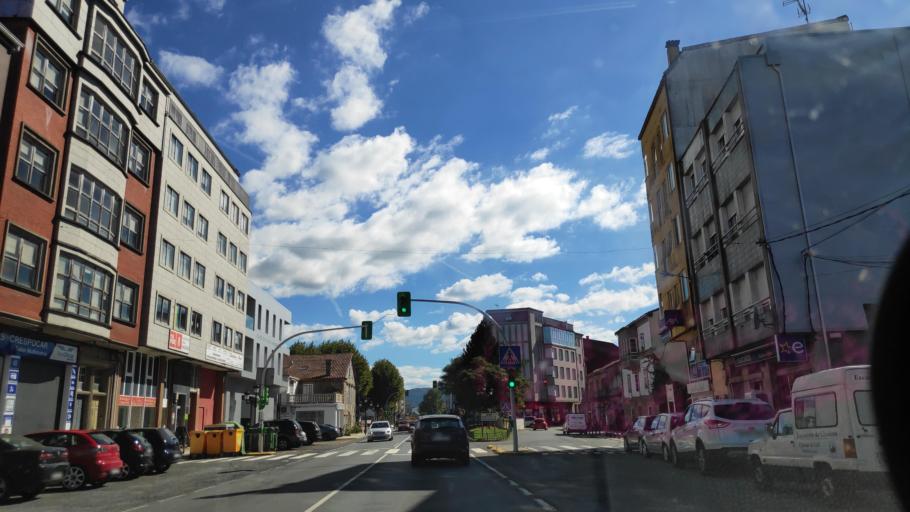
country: ES
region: Galicia
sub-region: Provincia da Coruna
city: Padron
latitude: 42.7401
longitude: -8.6587
